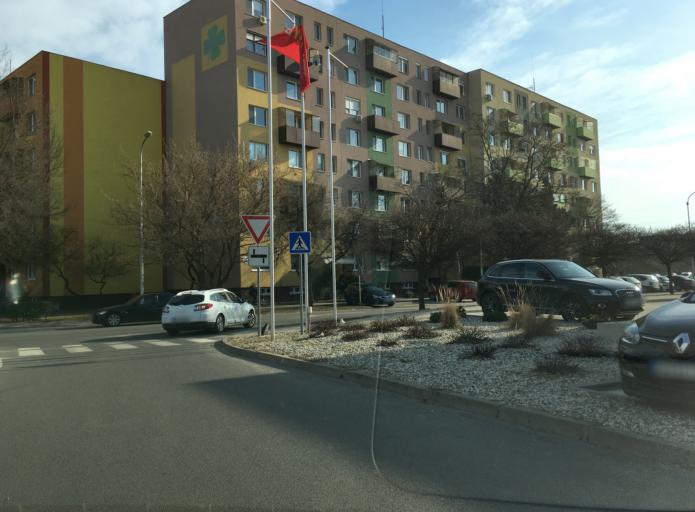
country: SK
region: Nitriansky
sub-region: Okres Nove Zamky
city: Nove Zamky
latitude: 47.9821
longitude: 18.1656
